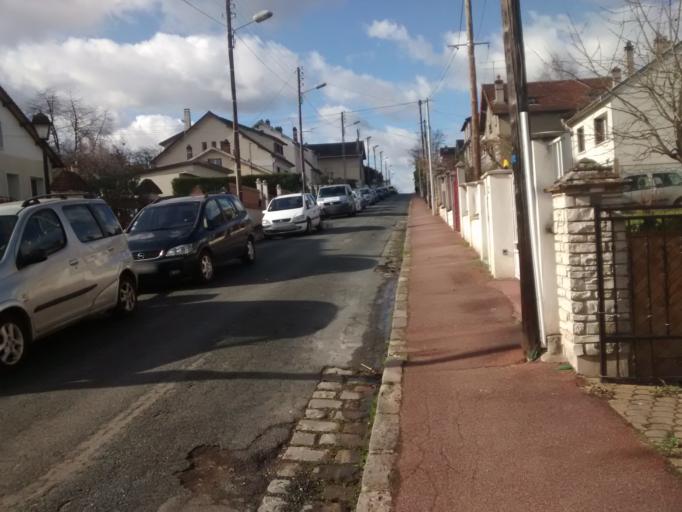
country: FR
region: Ile-de-France
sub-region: Departement de l'Essonne
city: Bures-sur-Yvette
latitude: 48.6936
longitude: 2.1557
